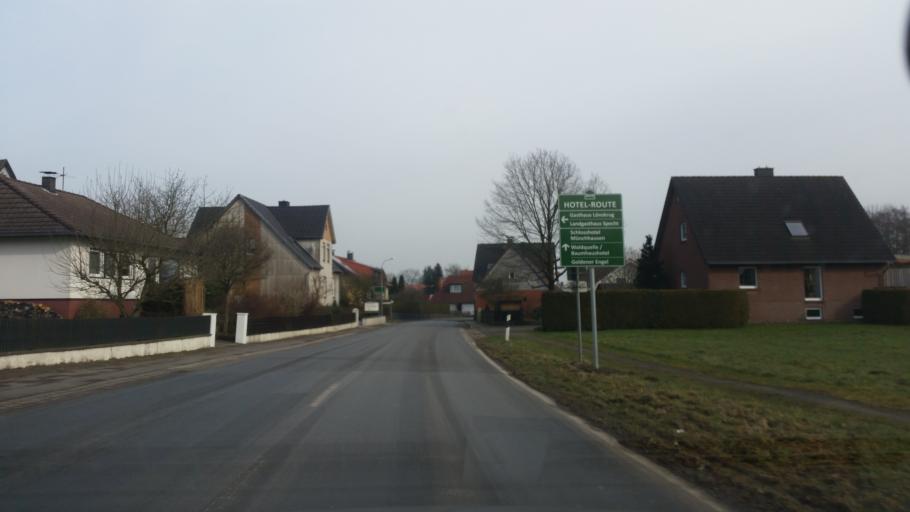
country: DE
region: Lower Saxony
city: Aerzen
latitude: 52.0728
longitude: 9.2186
